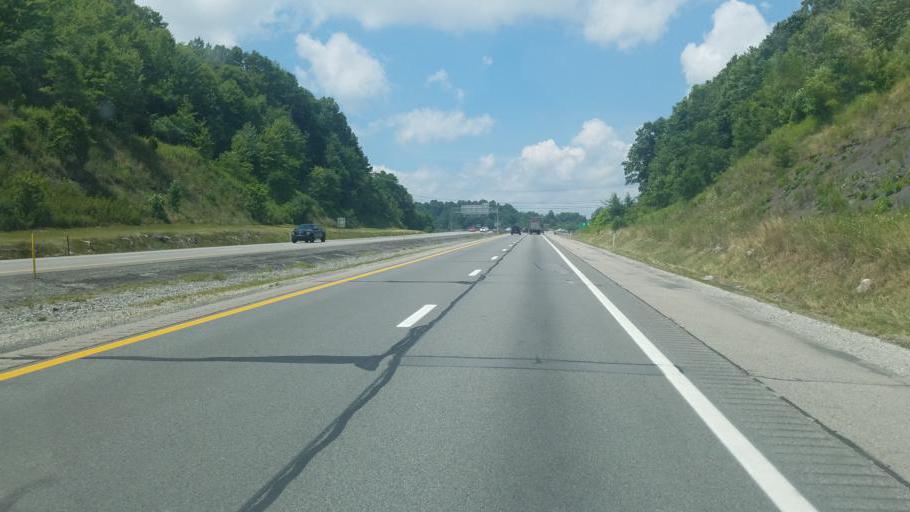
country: US
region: West Virginia
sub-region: Raleigh County
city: MacArthur
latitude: 37.7542
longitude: -81.2091
